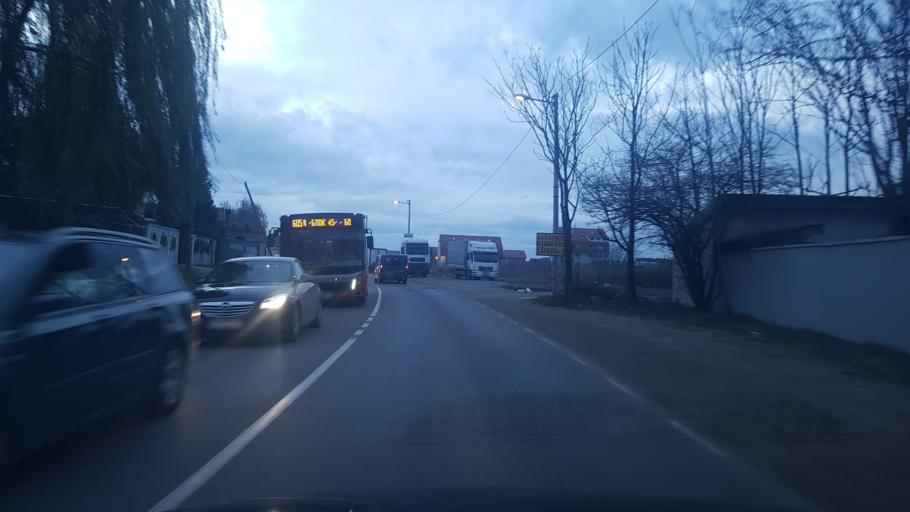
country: RS
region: Central Serbia
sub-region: Belgrade
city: Zemun
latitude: 44.8079
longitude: 20.3580
